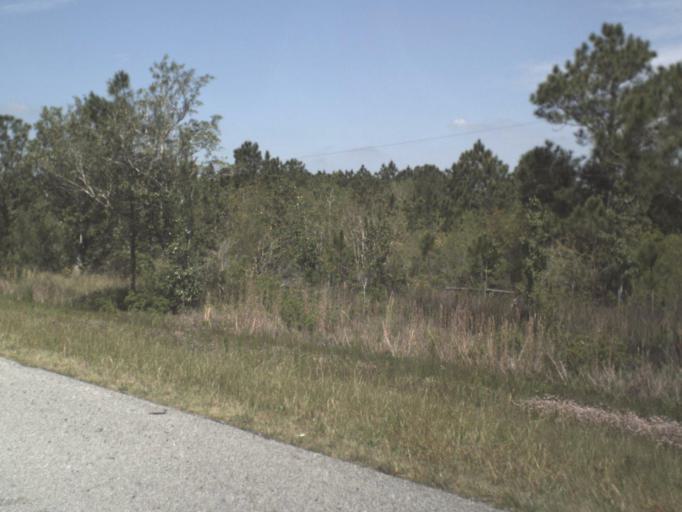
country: US
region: Florida
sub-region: Santa Rosa County
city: Pace
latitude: 30.5342
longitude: -87.1121
